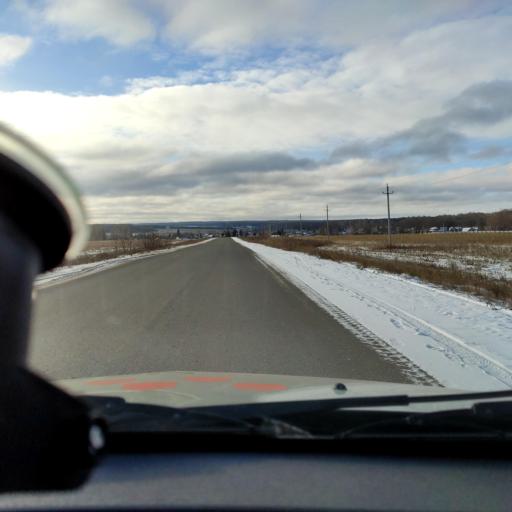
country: RU
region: Bashkortostan
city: Mikhaylovka
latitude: 54.8082
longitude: 55.7823
